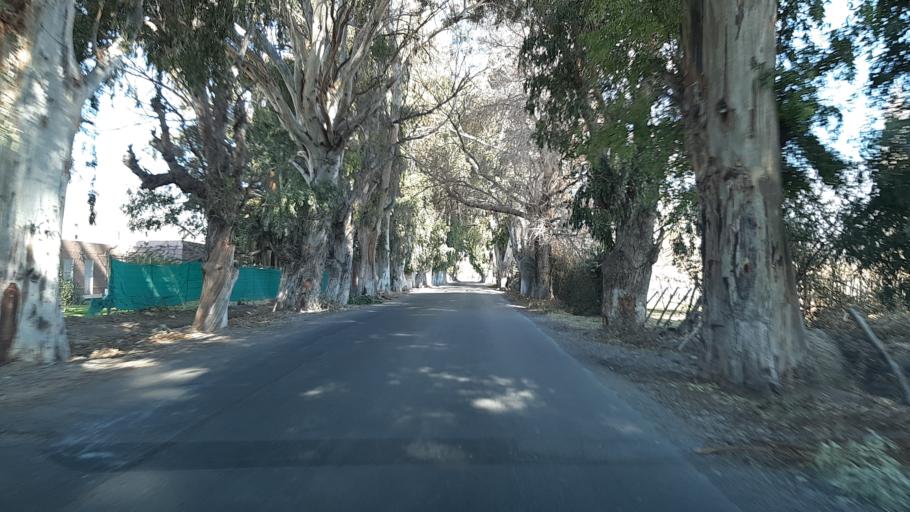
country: AR
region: San Juan
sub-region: Departamento de Zonda
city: Zonda
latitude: -31.5574
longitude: -68.7302
